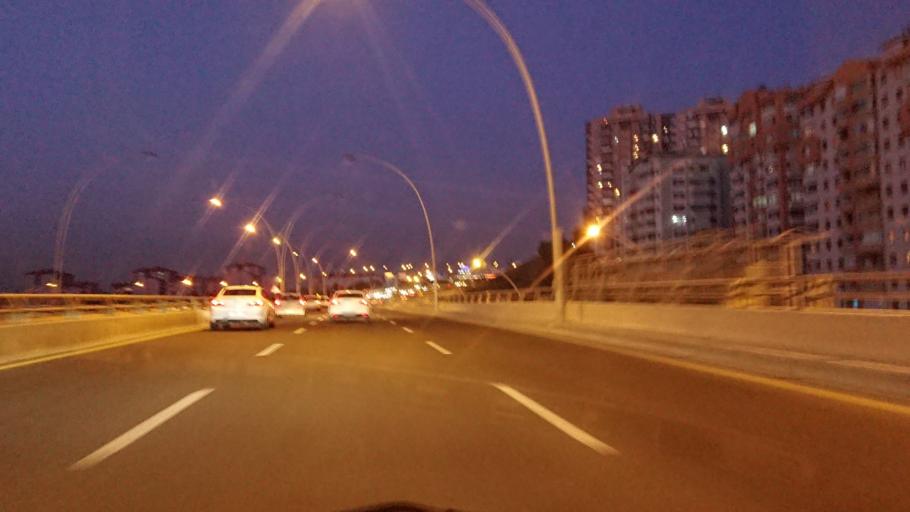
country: TR
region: Ankara
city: Batikent
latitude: 39.9024
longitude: 32.6917
